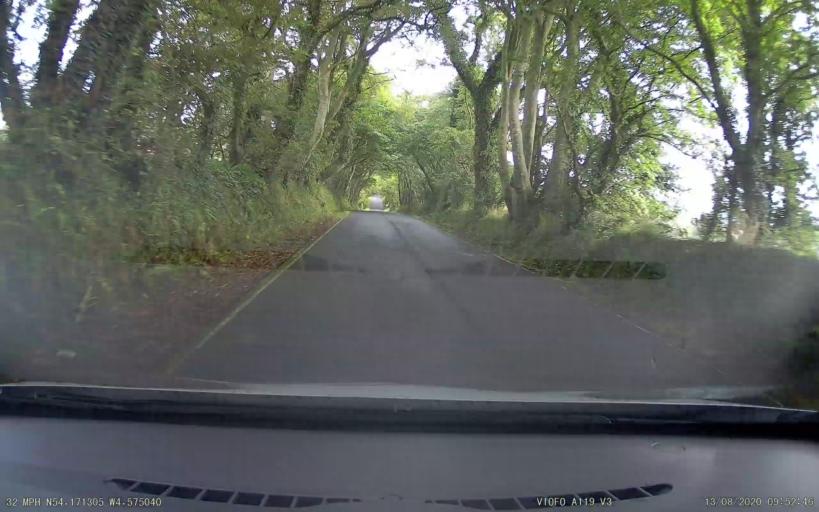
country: IM
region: Douglas
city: Douglas
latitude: 54.1713
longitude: -4.5750
